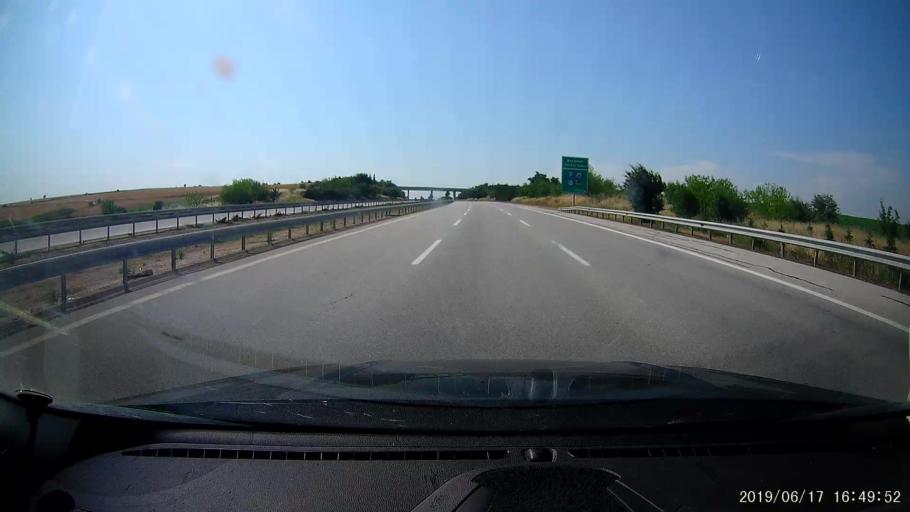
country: TR
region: Kirklareli
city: Babaeski
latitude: 41.5162
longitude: 27.1040
